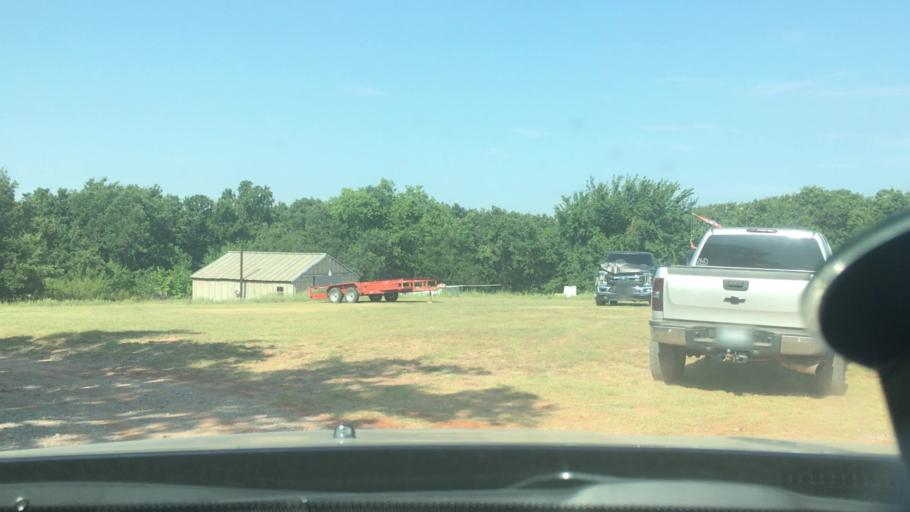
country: US
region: Oklahoma
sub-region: Garvin County
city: Lindsay
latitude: 34.7649
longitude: -97.6160
